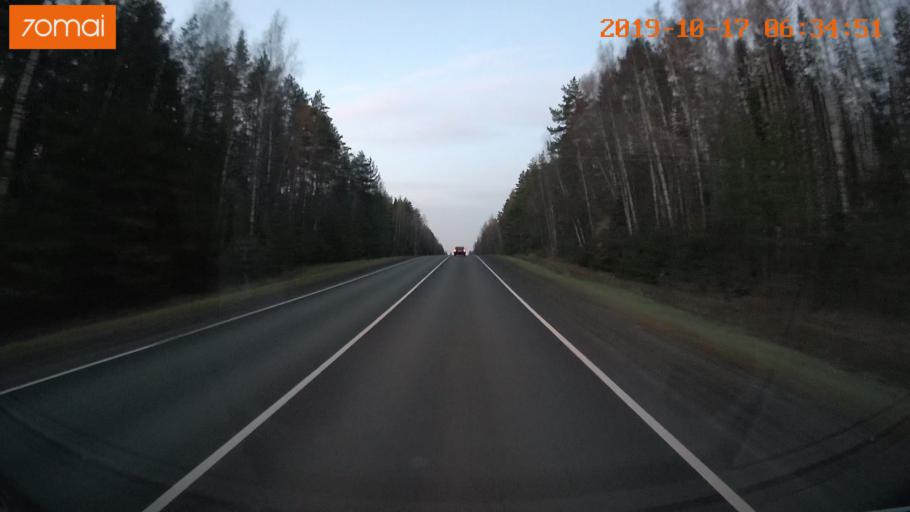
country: RU
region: Ivanovo
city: Novoye Leushino
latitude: 56.6987
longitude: 40.6315
